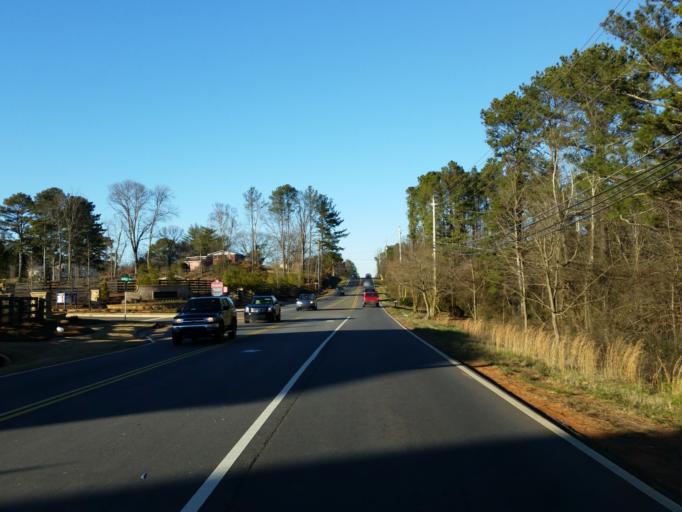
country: US
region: Georgia
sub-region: Cherokee County
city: Woodstock
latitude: 34.0772
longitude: -84.4848
